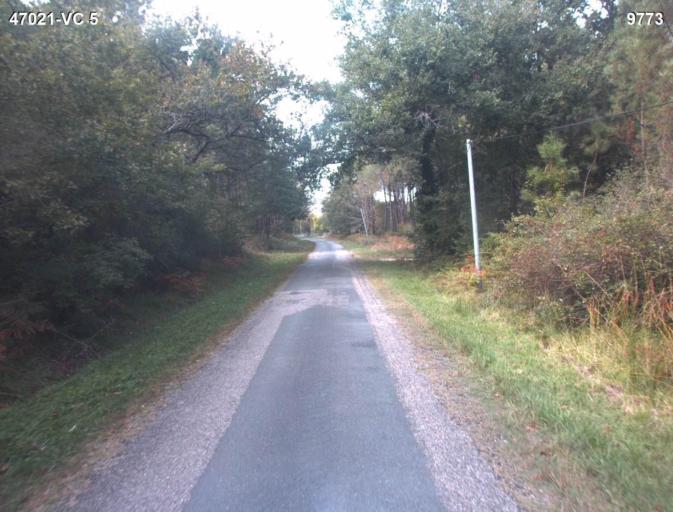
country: FR
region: Aquitaine
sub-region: Departement du Lot-et-Garonne
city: Barbaste
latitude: 44.1598
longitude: 0.1817
